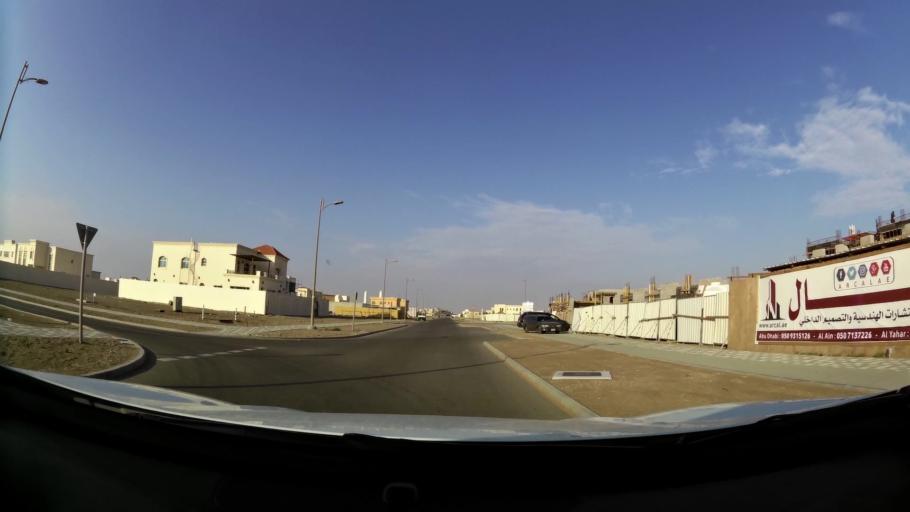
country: AE
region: Abu Dhabi
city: Al Ain
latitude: 24.1052
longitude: 55.8474
